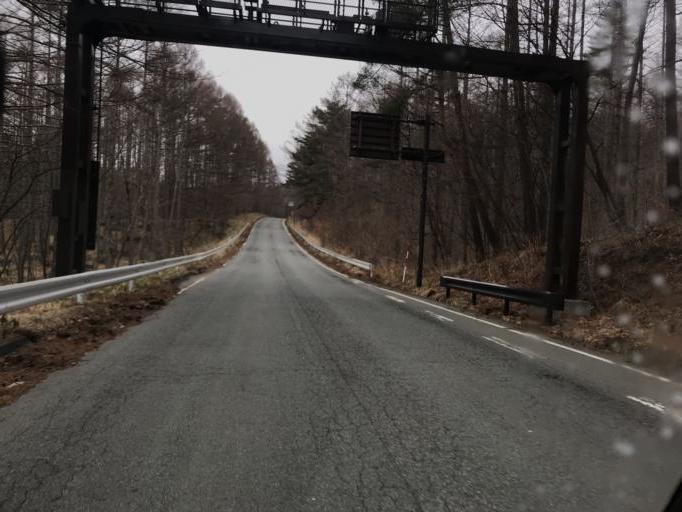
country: JP
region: Nagano
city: Chino
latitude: 35.8943
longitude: 138.3245
